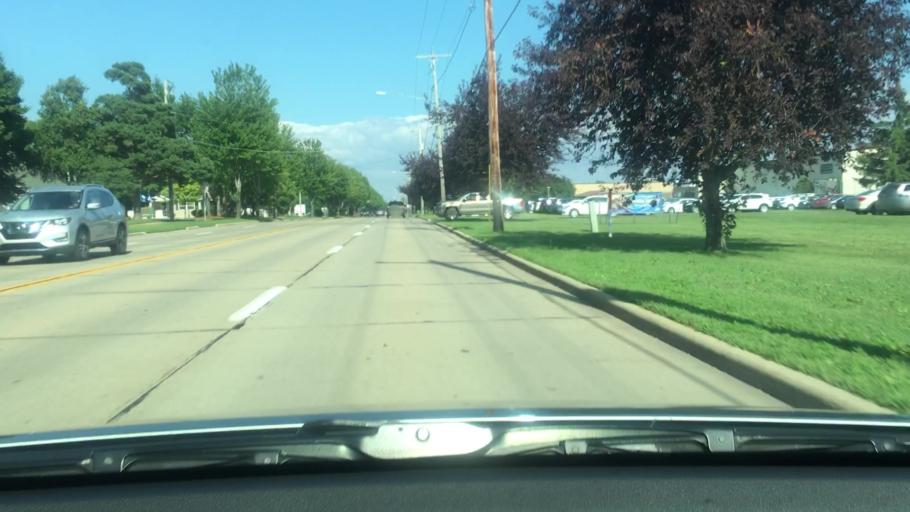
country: US
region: Wisconsin
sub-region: Winnebago County
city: Oshkosh
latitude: 43.9959
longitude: -88.5671
